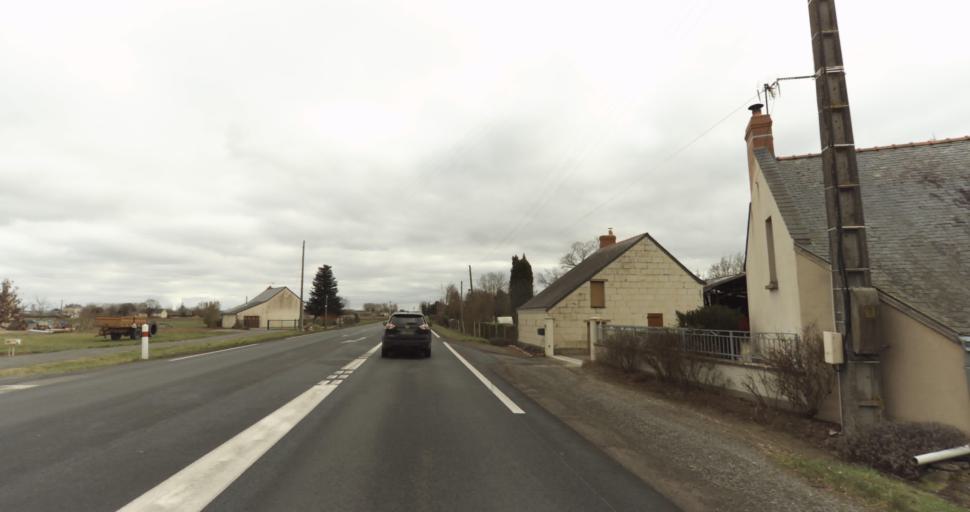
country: FR
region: Pays de la Loire
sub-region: Departement de Maine-et-Loire
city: Vivy
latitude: 47.3130
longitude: -0.0438
